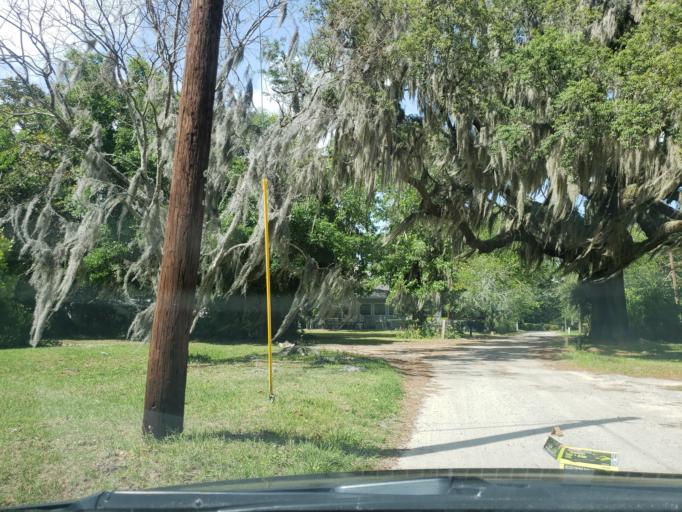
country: US
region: Georgia
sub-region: Chatham County
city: Thunderbolt
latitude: 32.0195
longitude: -81.0615
